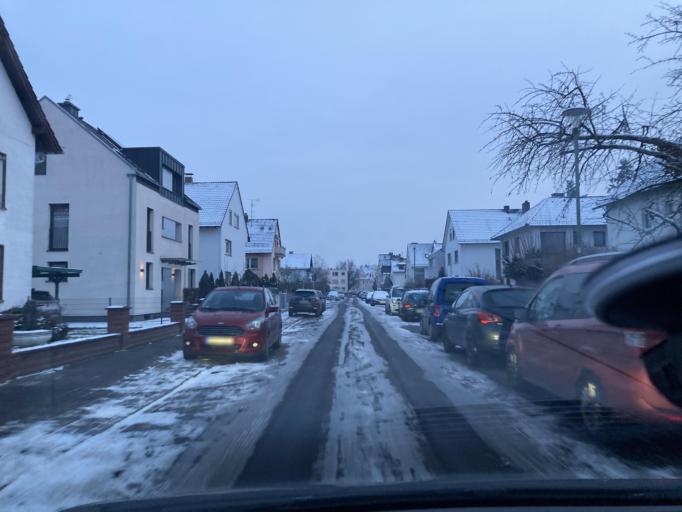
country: DE
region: Hesse
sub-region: Regierungsbezirk Darmstadt
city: Offenbach
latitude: 50.1227
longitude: 8.7855
